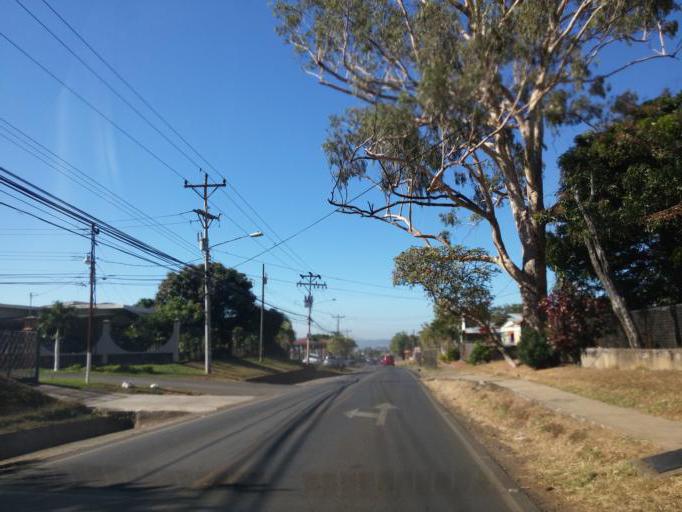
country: CR
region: Alajuela
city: Alajuela
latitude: 10.0304
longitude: -84.2148
